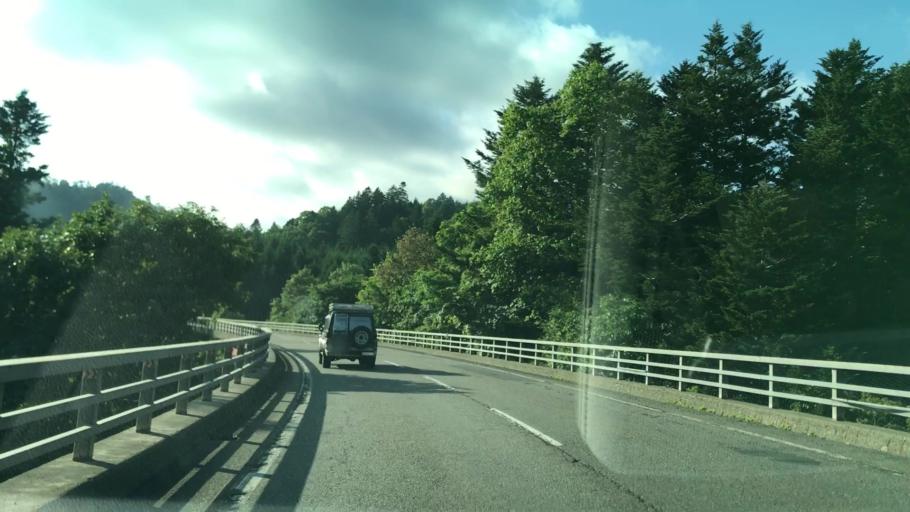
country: JP
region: Hokkaido
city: Iwamizawa
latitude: 42.9083
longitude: 142.1260
